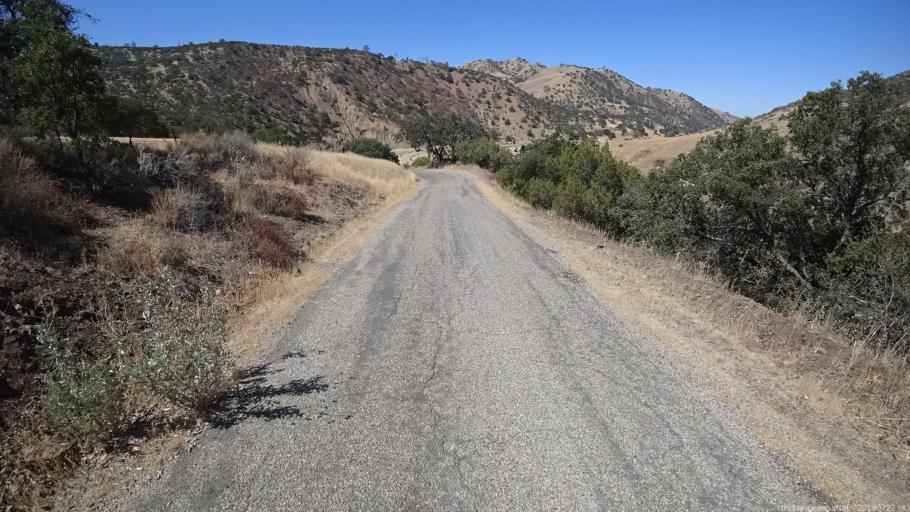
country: US
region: California
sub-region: Monterey County
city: King City
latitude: 36.2930
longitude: -120.8857
